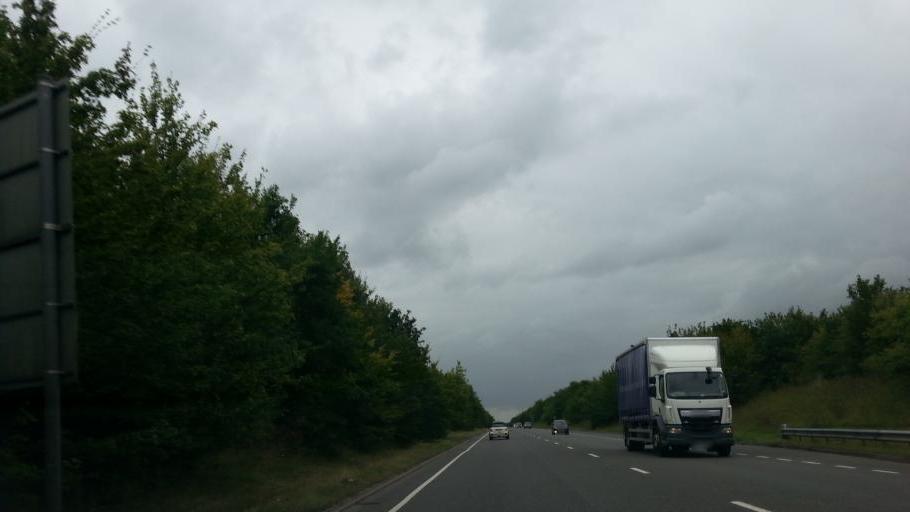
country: GB
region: England
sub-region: Essex
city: Chelmsford
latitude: 51.7793
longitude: 0.4878
